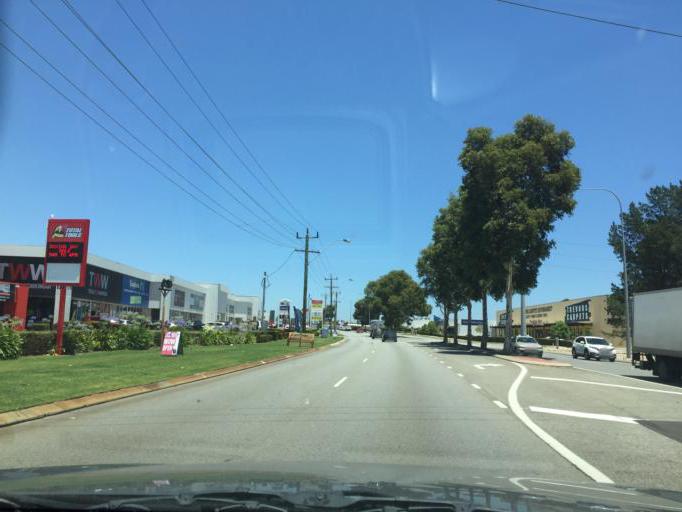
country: AU
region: Western Australia
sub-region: Canning
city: Canning Vale
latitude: -32.0590
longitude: 115.9094
